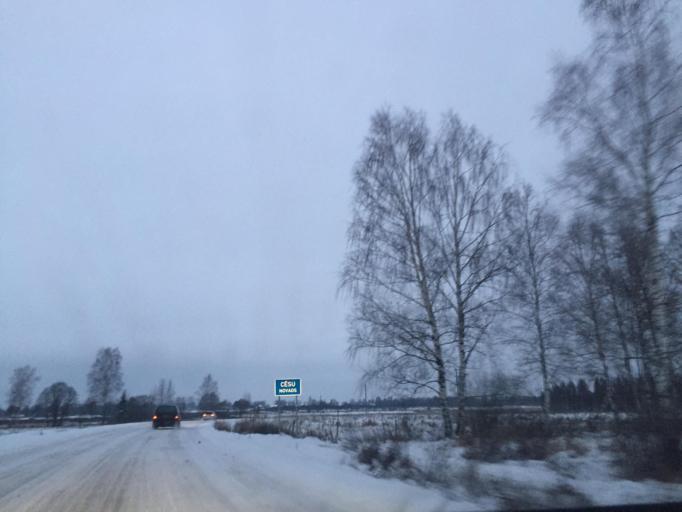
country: LV
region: Raunas
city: Rauna
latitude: 57.4264
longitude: 25.6403
